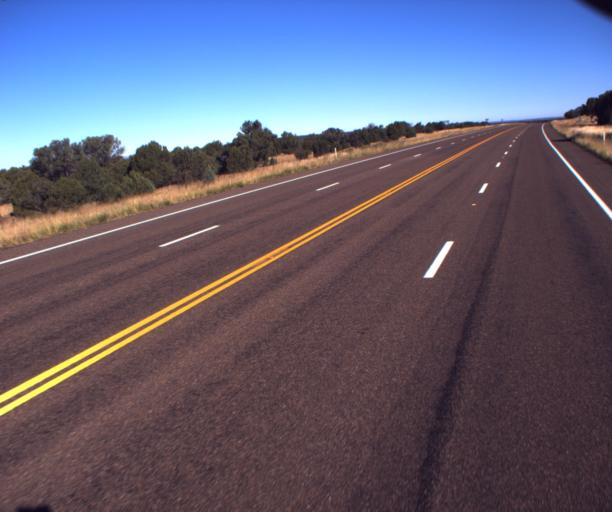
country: US
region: Arizona
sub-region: Navajo County
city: White Mountain Lake
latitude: 34.3494
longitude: -110.0531
